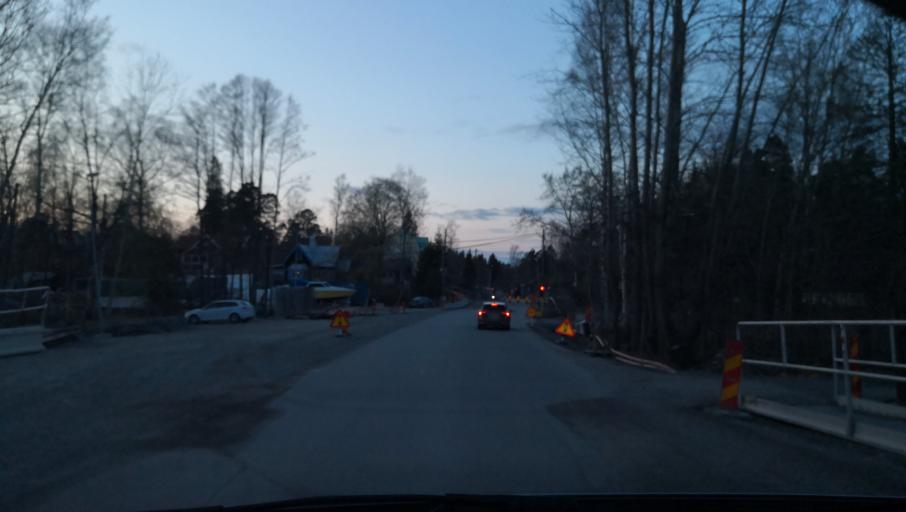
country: SE
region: Stockholm
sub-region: Nacka Kommun
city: Kummelnas
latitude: 59.3438
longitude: 18.2915
